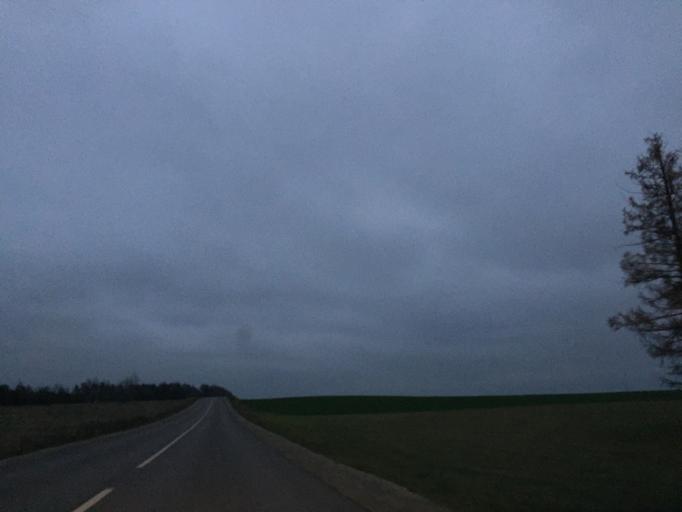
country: LV
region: Koceni
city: Koceni
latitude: 57.5516
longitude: 25.3332
